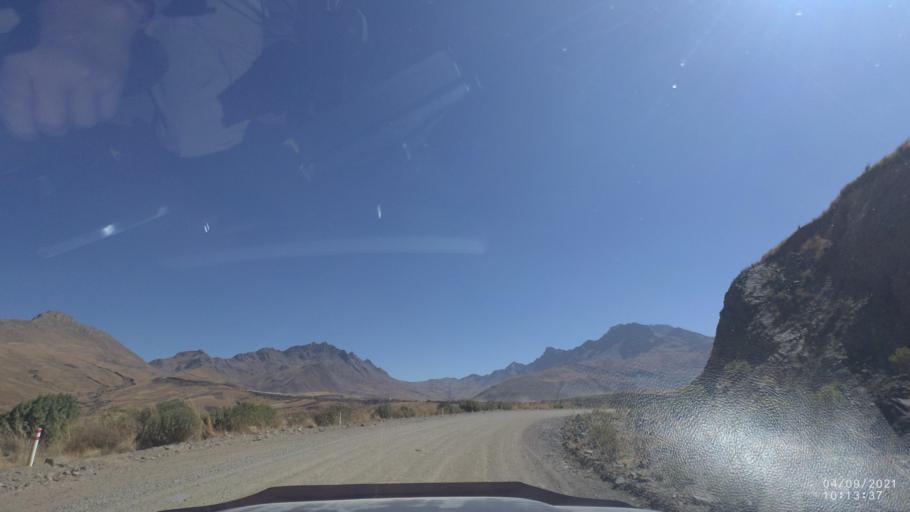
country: BO
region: Cochabamba
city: Sipe Sipe
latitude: -17.3357
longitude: -66.4068
